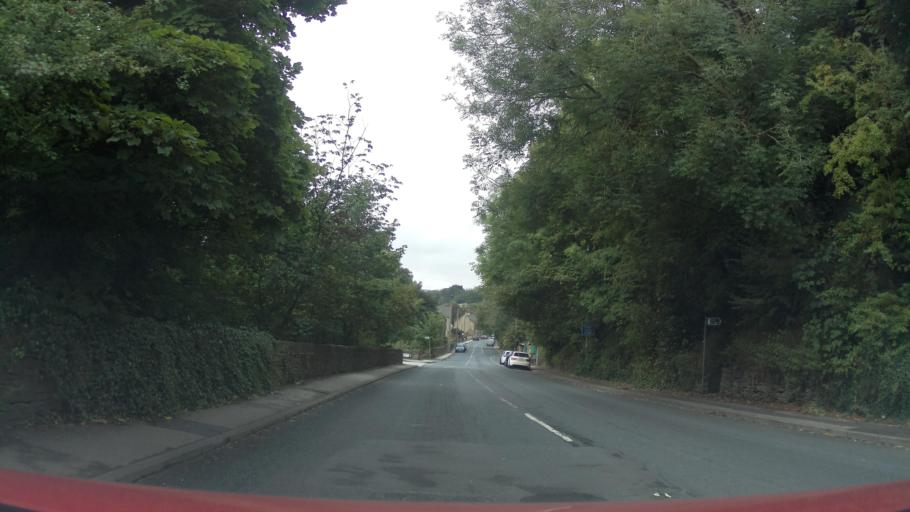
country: GB
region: England
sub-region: Kirklees
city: Holmfirth
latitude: 53.5673
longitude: -1.7958
